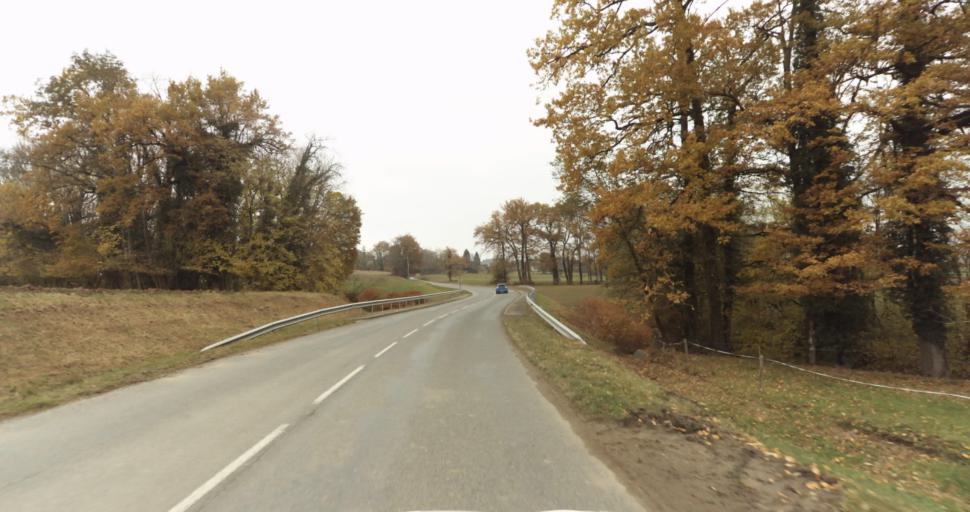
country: FR
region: Rhone-Alpes
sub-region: Departement de la Haute-Savoie
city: Alby-sur-Cheran
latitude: 45.7906
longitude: 6.0116
